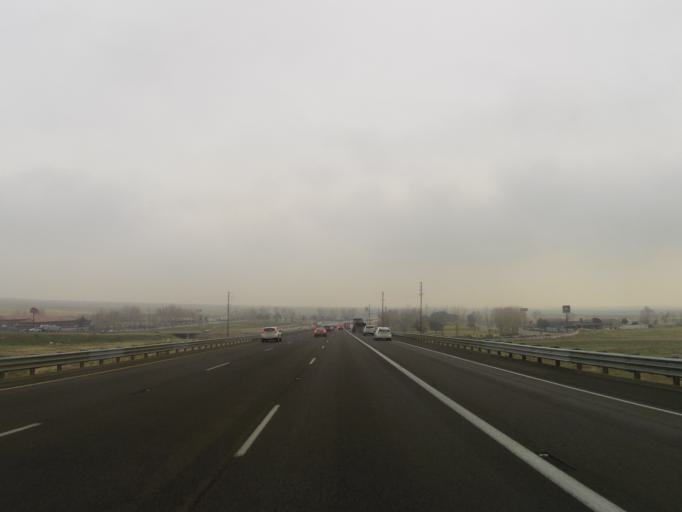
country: US
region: California
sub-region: Kern County
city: Lebec
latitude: 34.9372
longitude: -118.9282
